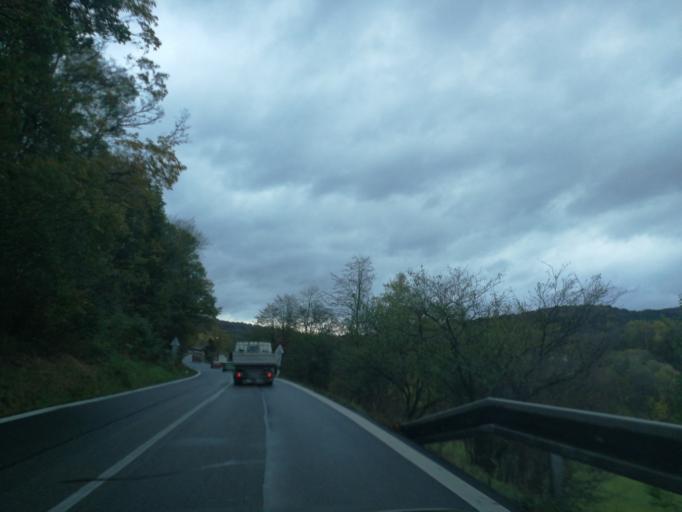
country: CZ
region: Zlin
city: Valasske Mezirici
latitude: 49.4986
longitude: 17.9926
